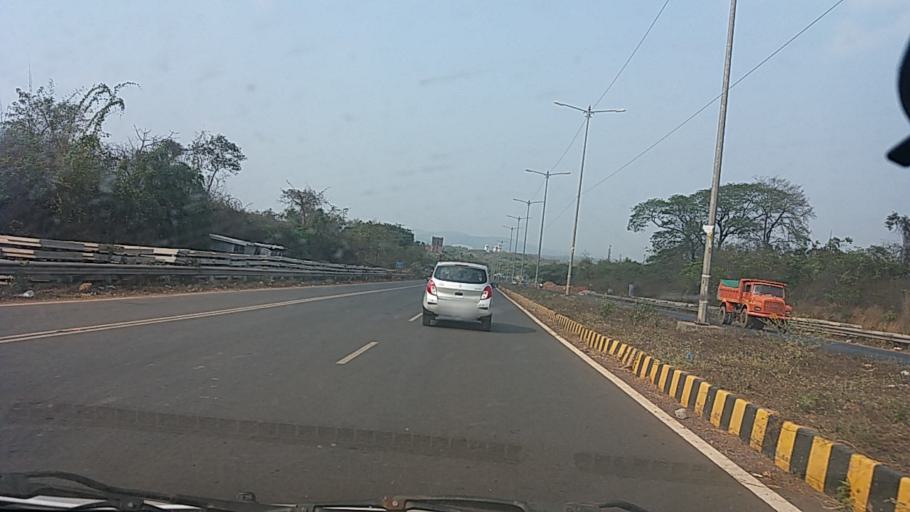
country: IN
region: Goa
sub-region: North Goa
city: Jua
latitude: 15.4943
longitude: 73.9089
